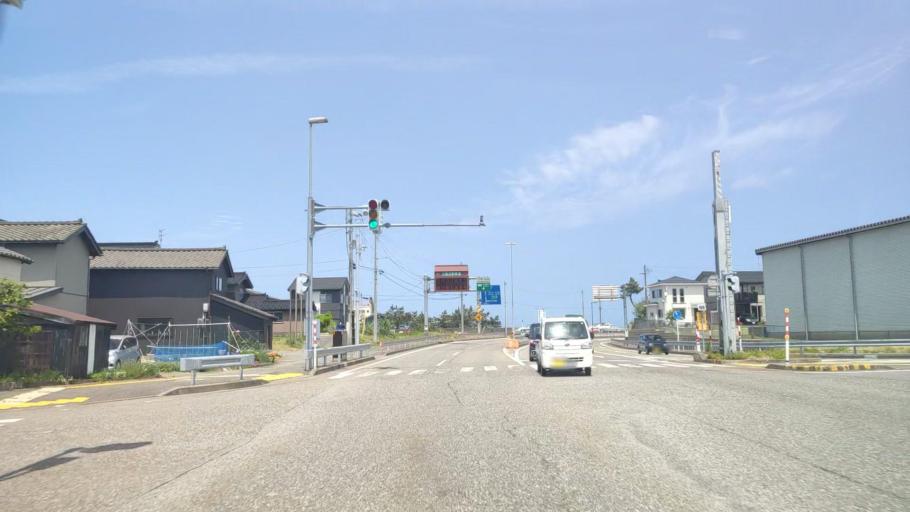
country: JP
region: Niigata
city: Itoigawa
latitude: 37.0421
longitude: 137.8464
